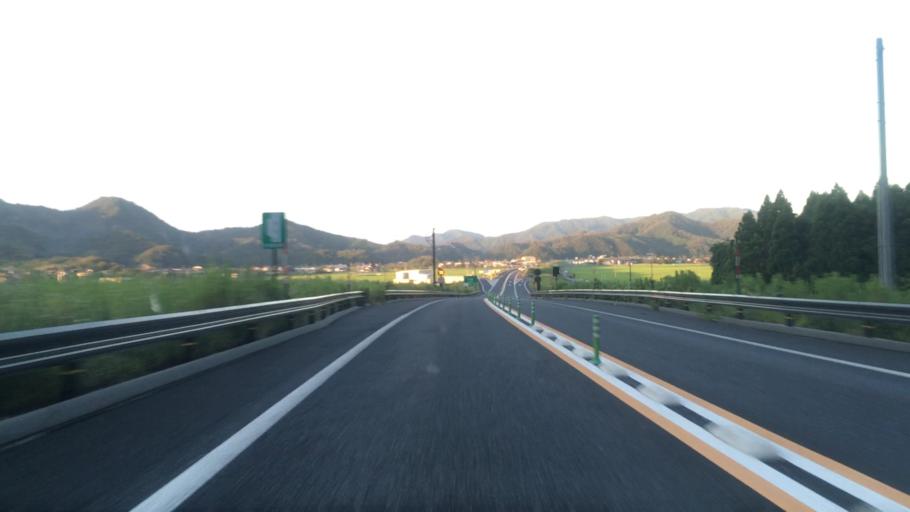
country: JP
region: Tottori
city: Tottori
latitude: 35.5680
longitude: 134.2932
